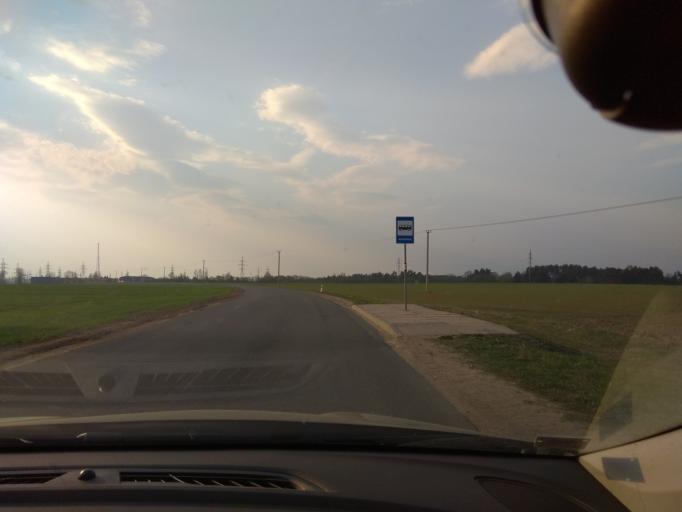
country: LT
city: Baltoji Voke
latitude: 54.6085
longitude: 25.1291
